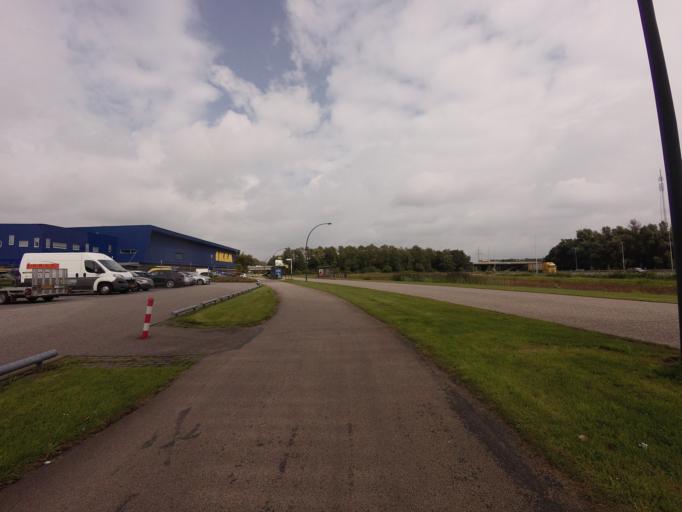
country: NL
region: Overijssel
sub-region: Gemeente Borne
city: Borne
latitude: 52.2873
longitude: 6.7683
